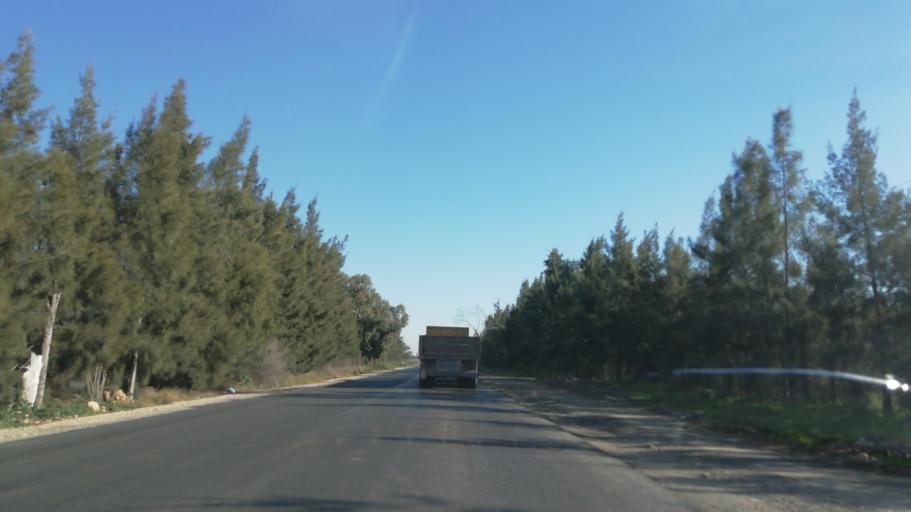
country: DZ
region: Relizane
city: Zemoura
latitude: 35.7580
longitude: 0.6674
